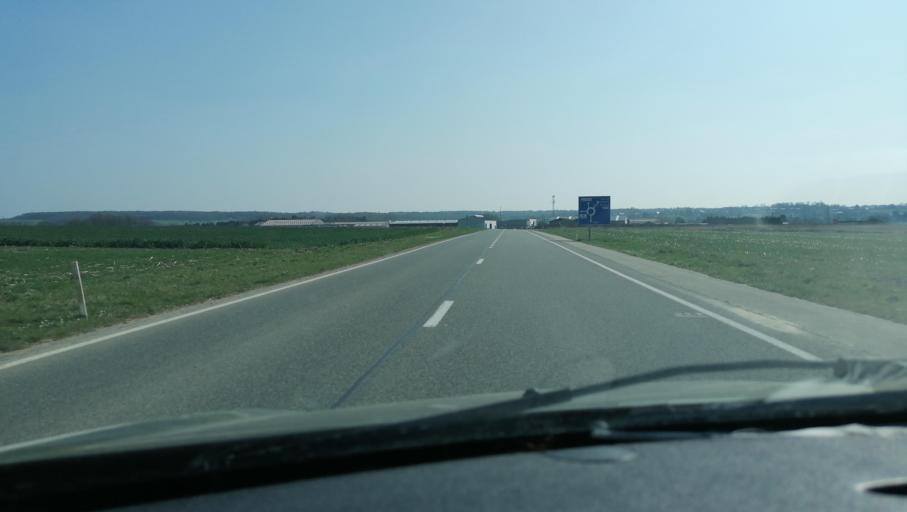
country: BE
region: Wallonia
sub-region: Province du Hainaut
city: Chimay
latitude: 50.0428
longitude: 4.3782
